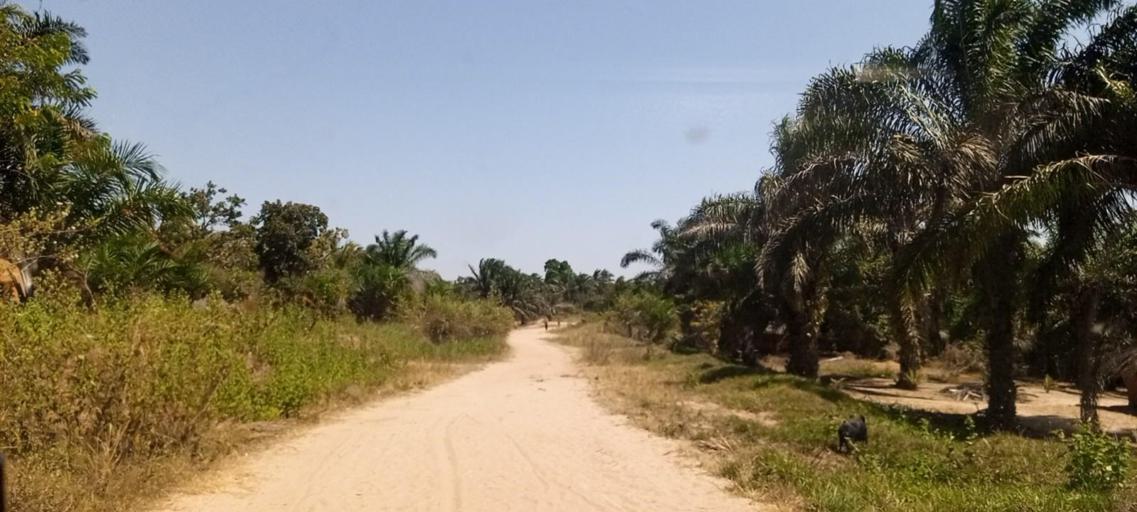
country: CD
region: Kasai-Oriental
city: Kabinda
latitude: -5.9629
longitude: 24.7714
